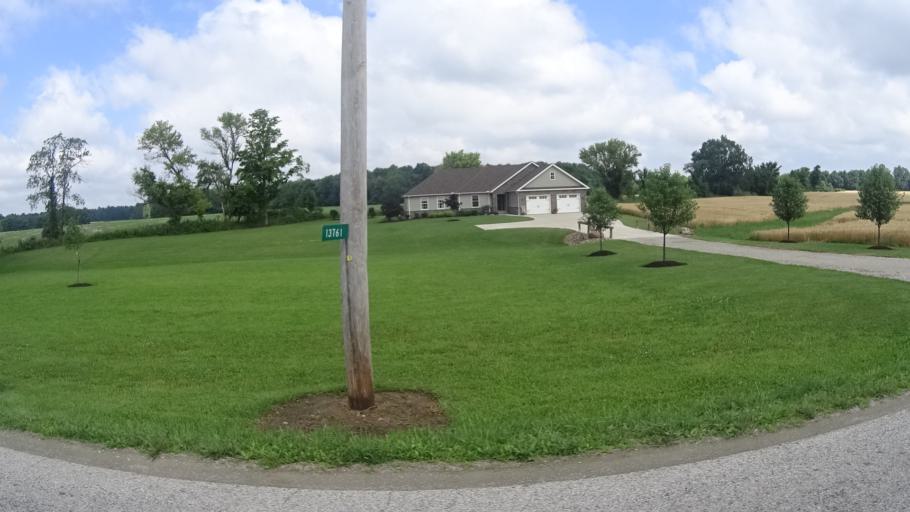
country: US
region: Ohio
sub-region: Huron County
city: Wakeman
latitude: 41.2930
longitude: -82.3920
